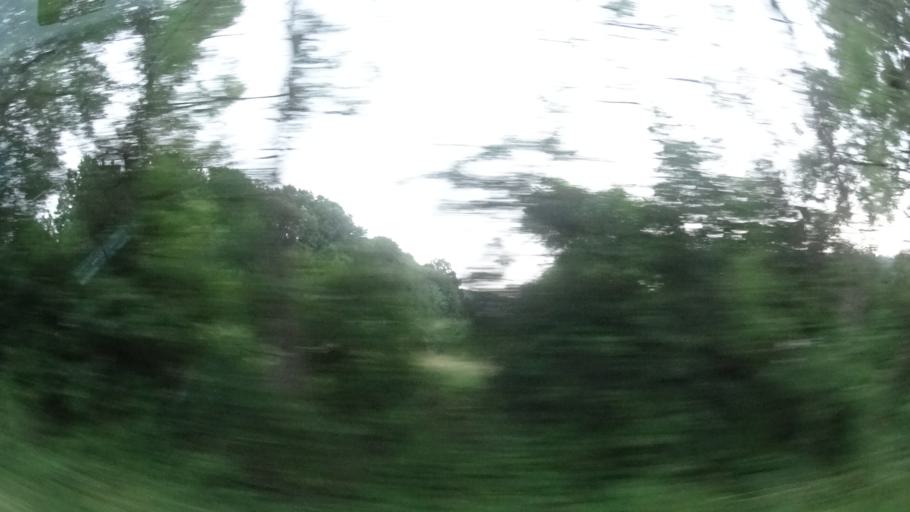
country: DE
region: Lower Saxony
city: Heyen
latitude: 52.0593
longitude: 9.5270
